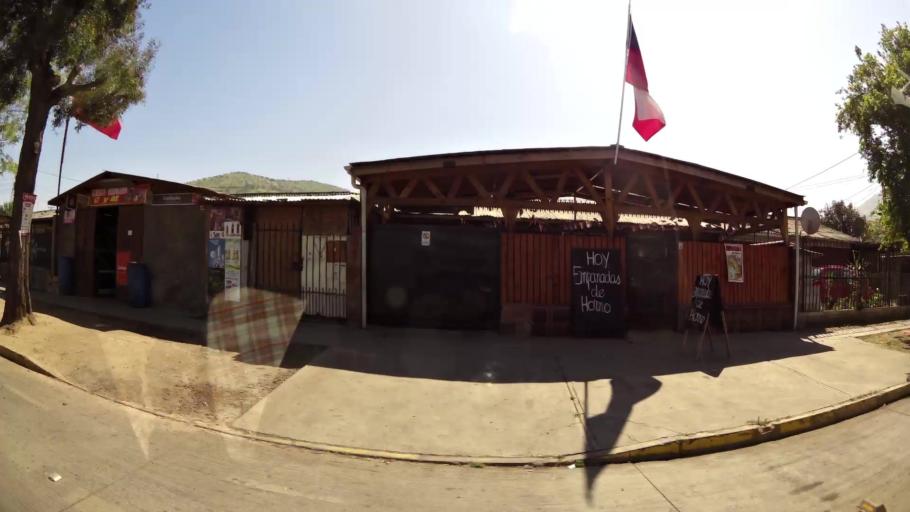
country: CL
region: Santiago Metropolitan
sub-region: Provincia de Santiago
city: Lo Prado
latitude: -33.4019
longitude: -70.7293
